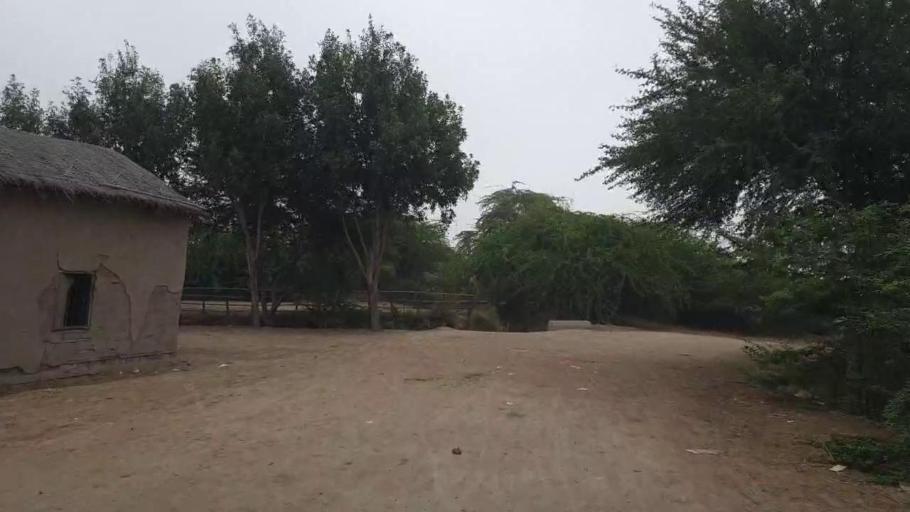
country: PK
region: Sindh
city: Badin
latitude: 24.5961
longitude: 68.6769
